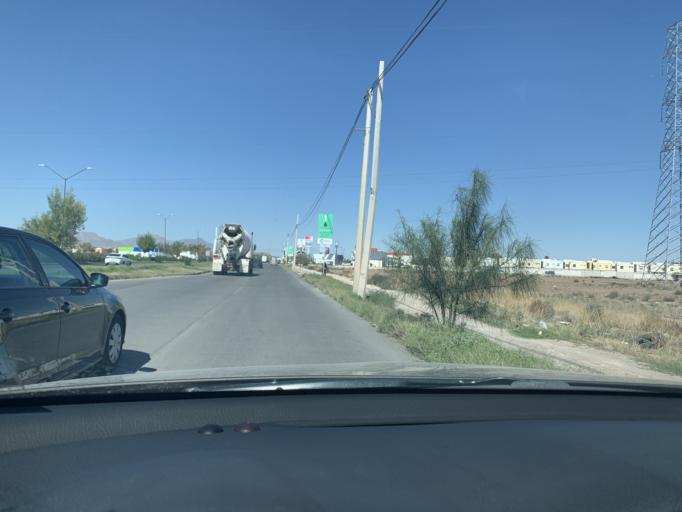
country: US
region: Texas
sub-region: El Paso County
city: Socorro
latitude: 31.6972
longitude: -106.3817
